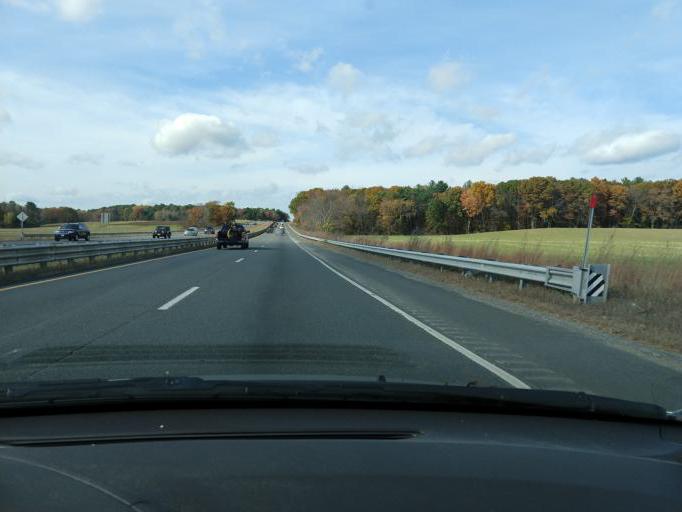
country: US
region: Massachusetts
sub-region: Middlesex County
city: West Concord
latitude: 42.4702
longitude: -71.4139
